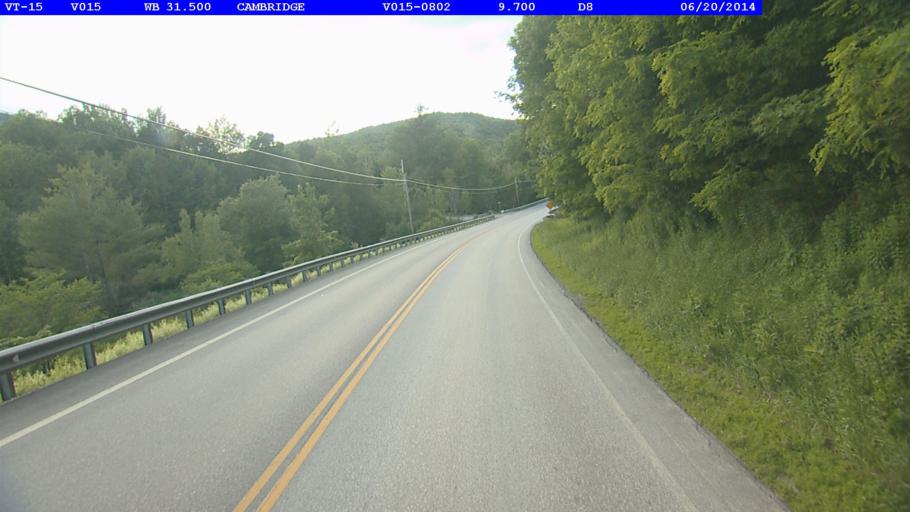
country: US
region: Vermont
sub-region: Lamoille County
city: Johnson
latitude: 44.6506
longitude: -72.7574
